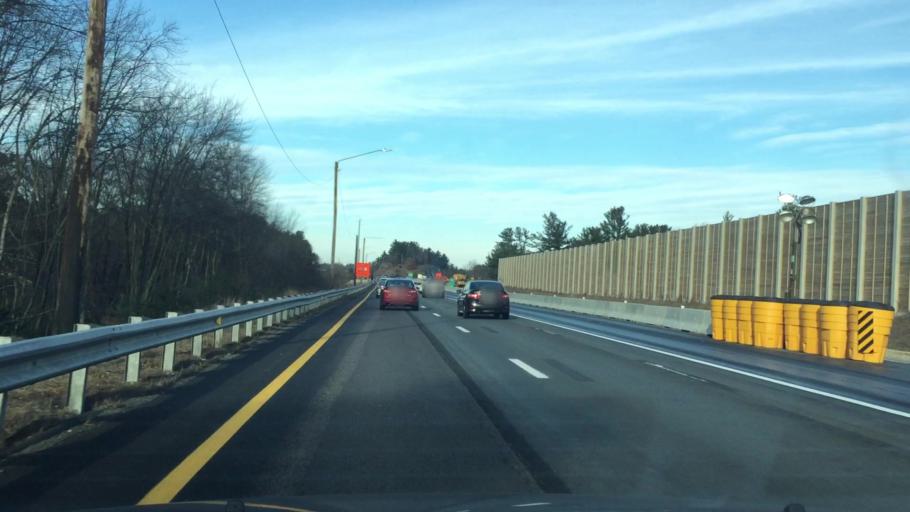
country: US
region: New Hampshire
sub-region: Hillsborough County
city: Manchester
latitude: 42.9514
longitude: -71.3992
